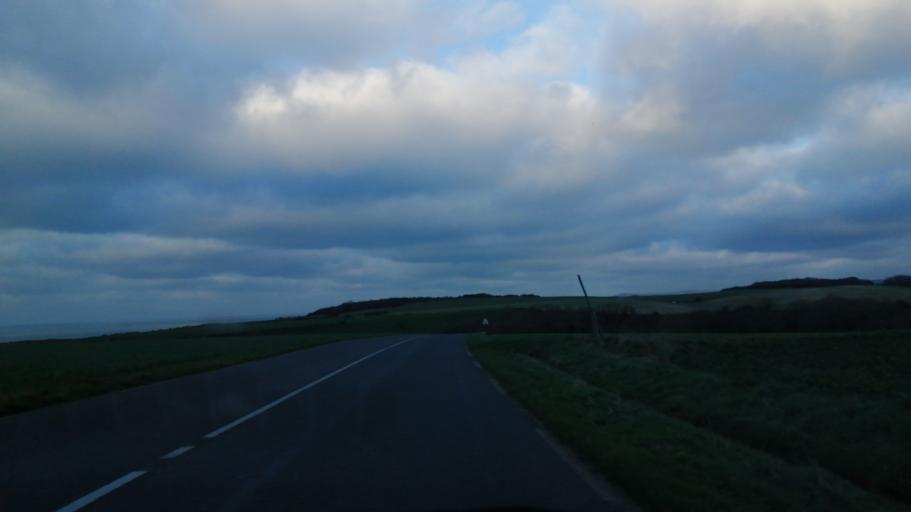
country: FR
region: Nord-Pas-de-Calais
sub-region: Departement du Pas-de-Calais
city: Ambleteuse
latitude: 50.8565
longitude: 1.6156
